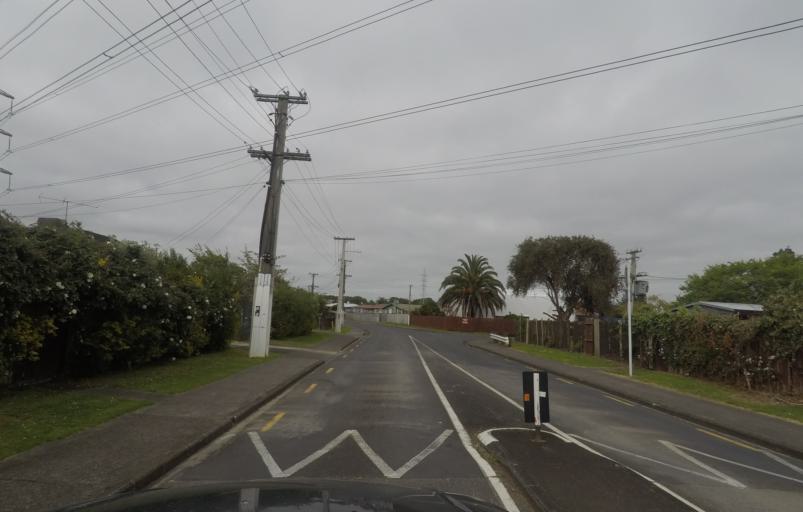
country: NZ
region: Auckland
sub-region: Auckland
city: Manukau City
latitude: -36.9576
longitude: 174.8644
